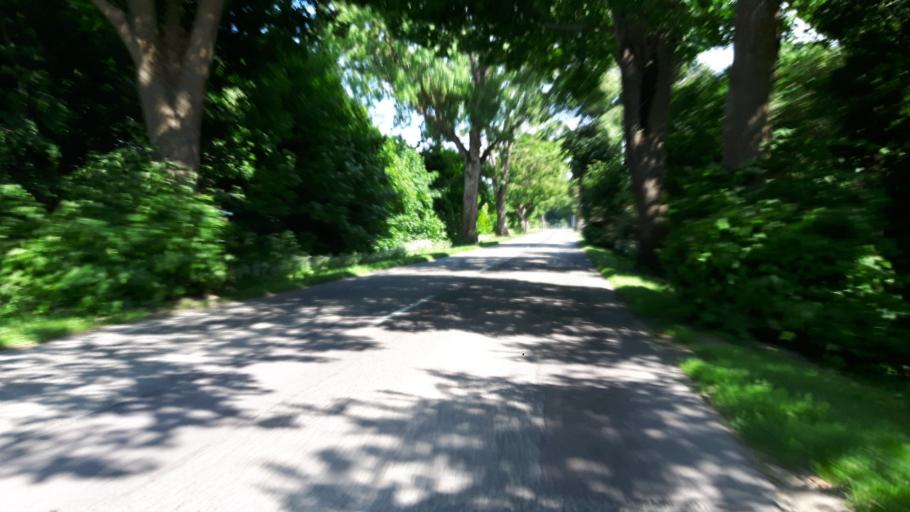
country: PL
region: Pomeranian Voivodeship
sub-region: Powiat wejherowski
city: Orle
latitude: 54.6485
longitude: 18.1062
